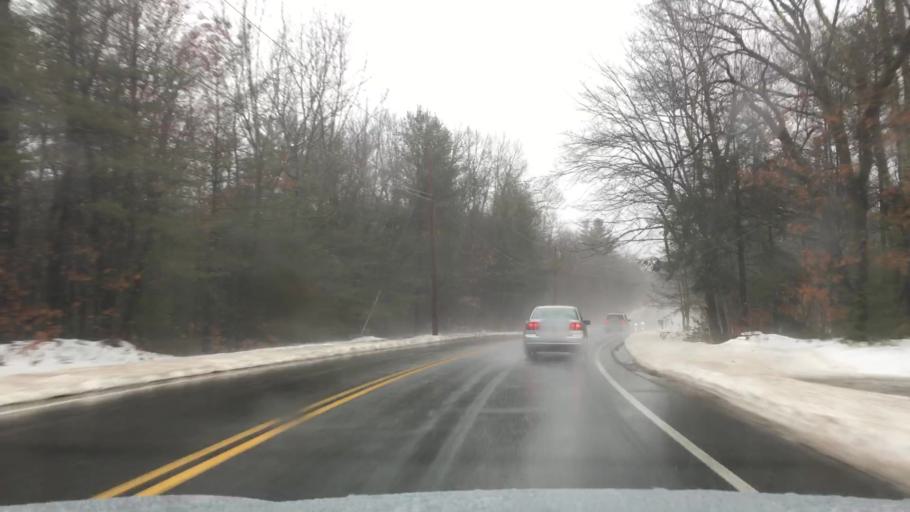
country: US
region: Massachusetts
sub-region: Hampshire County
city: Granby
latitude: 42.2348
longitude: -72.4859
